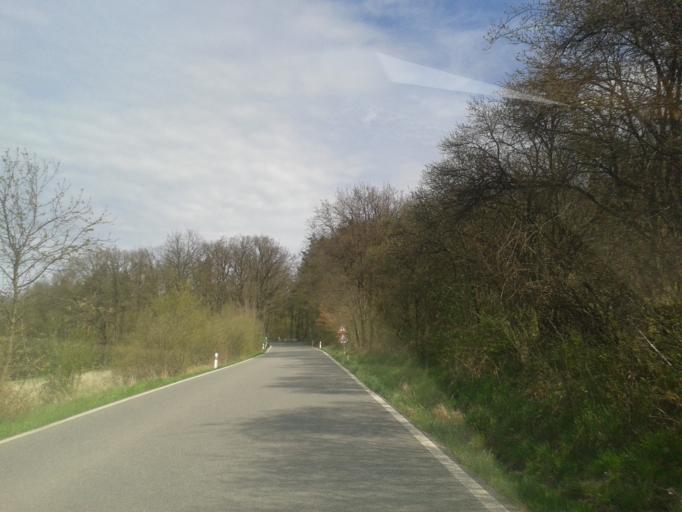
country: CZ
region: Central Bohemia
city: Revnice
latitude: 49.9038
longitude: 14.2309
